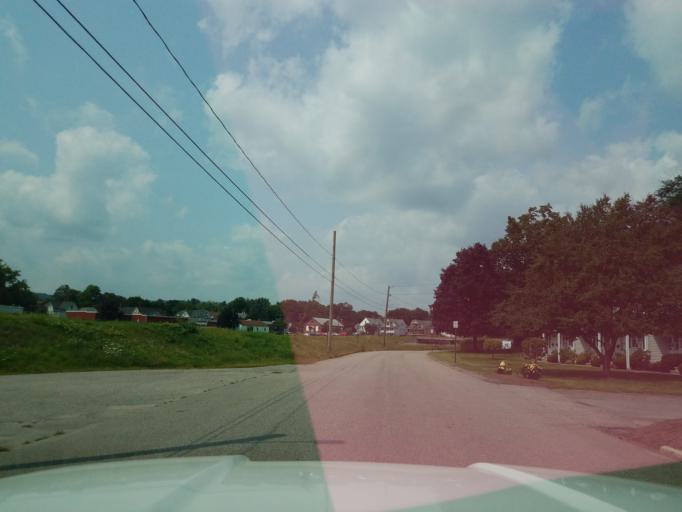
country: US
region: Connecticut
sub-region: Litchfield County
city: Torrington
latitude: 41.7942
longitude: -73.1162
